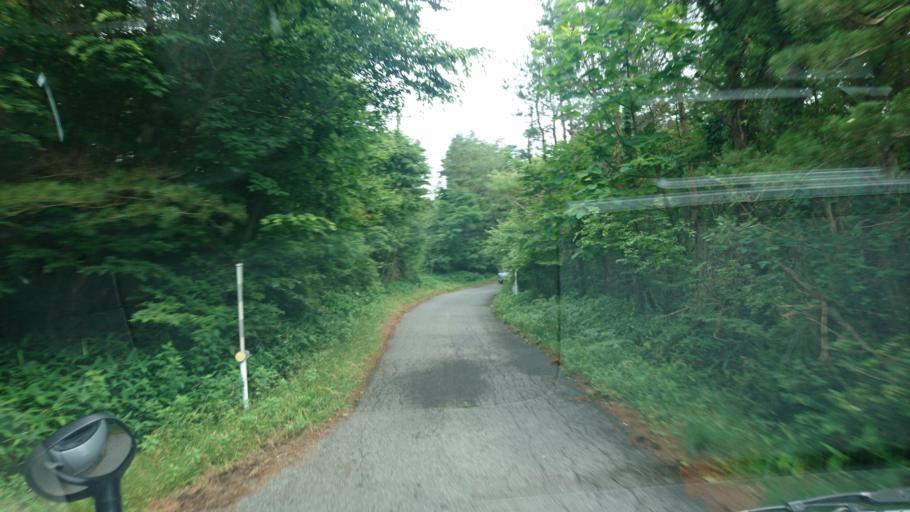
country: JP
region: Iwate
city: Ofunato
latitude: 39.1390
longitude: 141.7547
